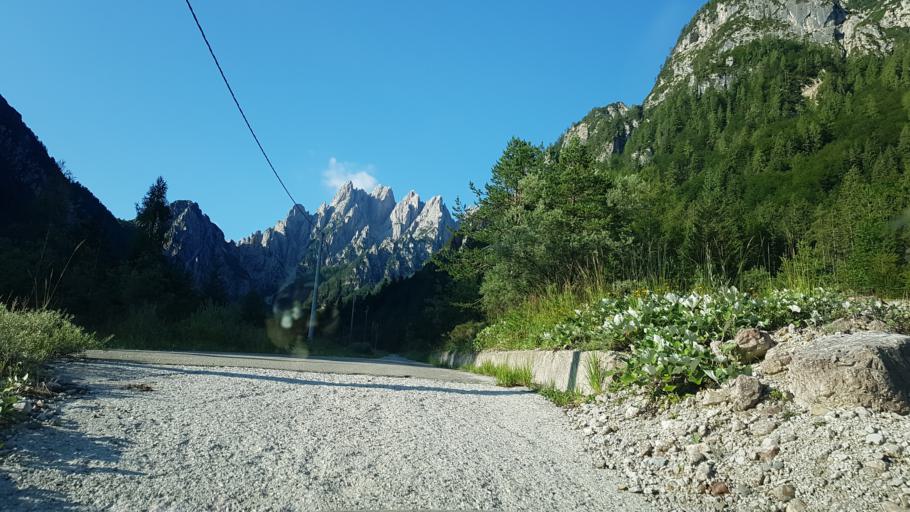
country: IT
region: Friuli Venezia Giulia
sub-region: Provincia di Udine
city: Pontebba
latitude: 46.5004
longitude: 13.2540
